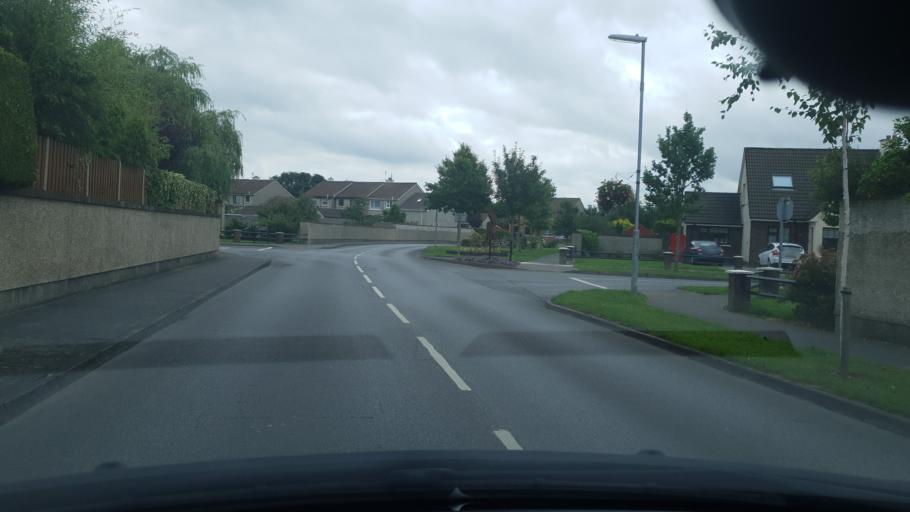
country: IE
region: Munster
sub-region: Ciarrai
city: Tralee
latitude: 52.2596
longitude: -9.6859
